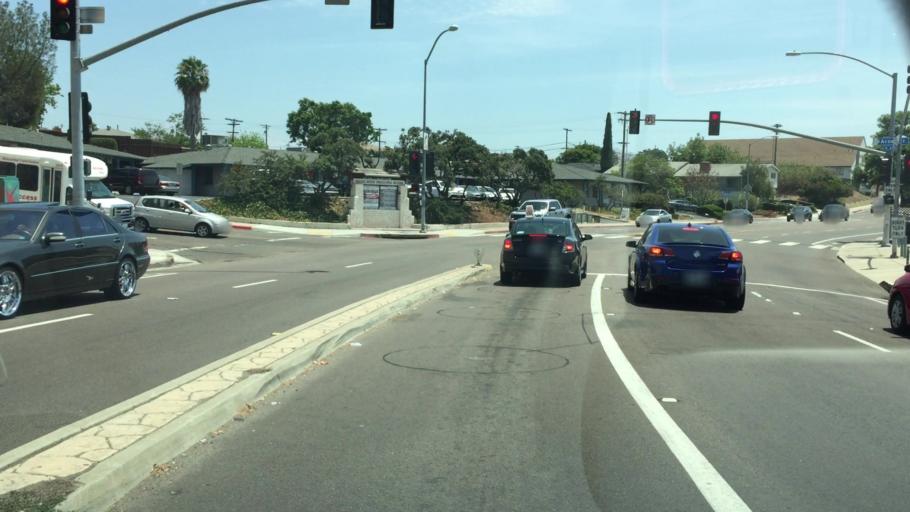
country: US
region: California
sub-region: San Diego County
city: Lemon Grove
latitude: 32.7599
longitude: -117.0666
